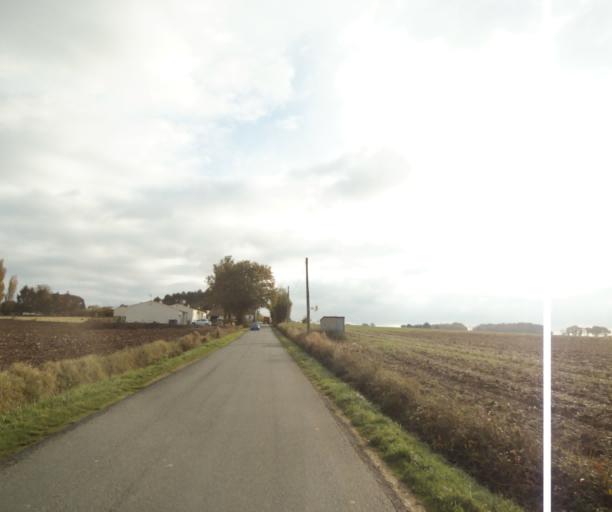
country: FR
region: Poitou-Charentes
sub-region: Departement de la Charente-Maritime
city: Saint-Georges-des-Coteaux
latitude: 45.7792
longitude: -0.7238
